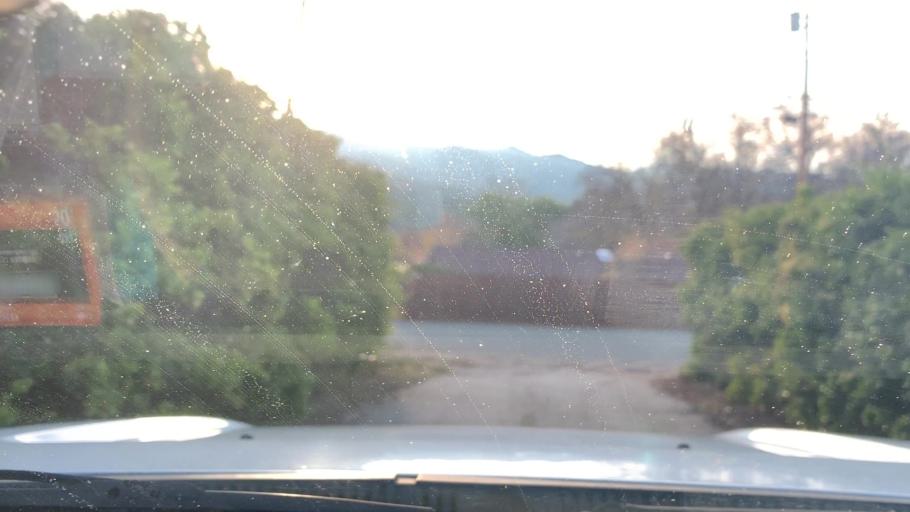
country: US
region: California
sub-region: San Luis Obispo County
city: Santa Margarita
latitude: 35.4361
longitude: -120.6344
